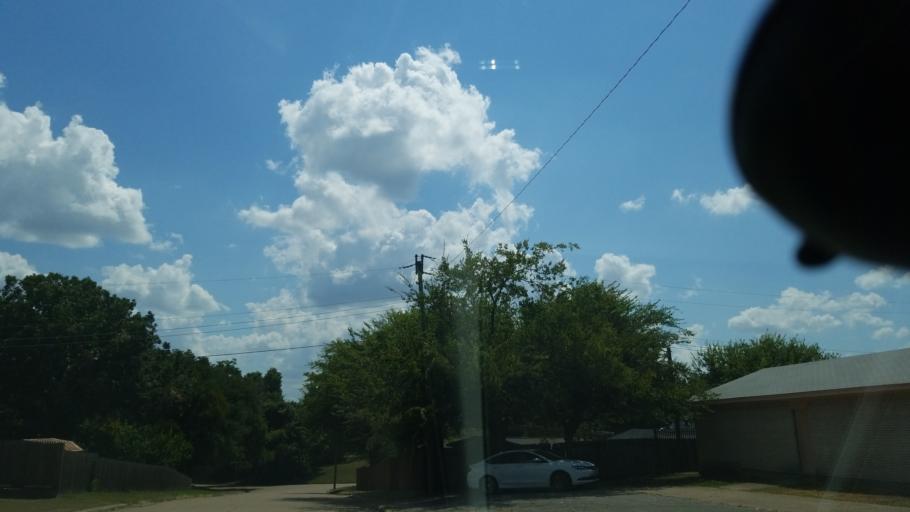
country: US
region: Texas
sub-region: Dallas County
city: Grand Prairie
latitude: 32.7284
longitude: -96.9926
